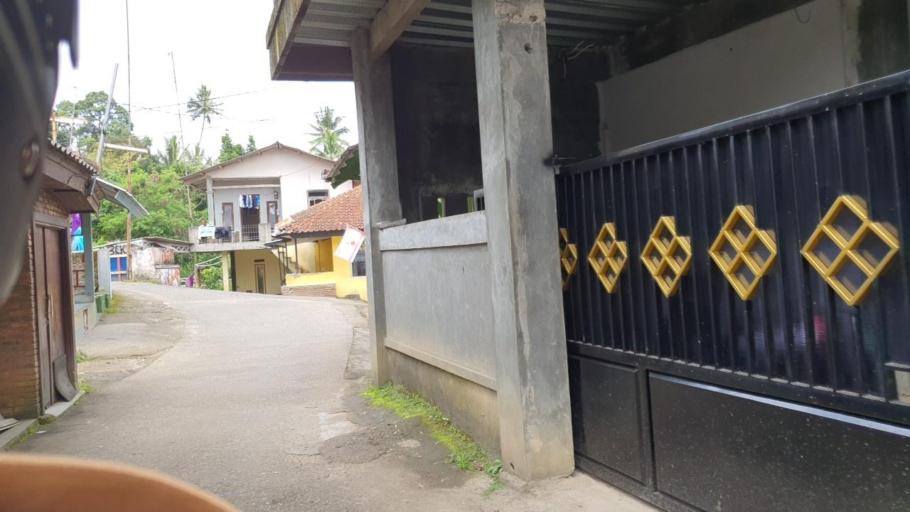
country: ID
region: West Java
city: Caringin
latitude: -6.6478
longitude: 106.8880
